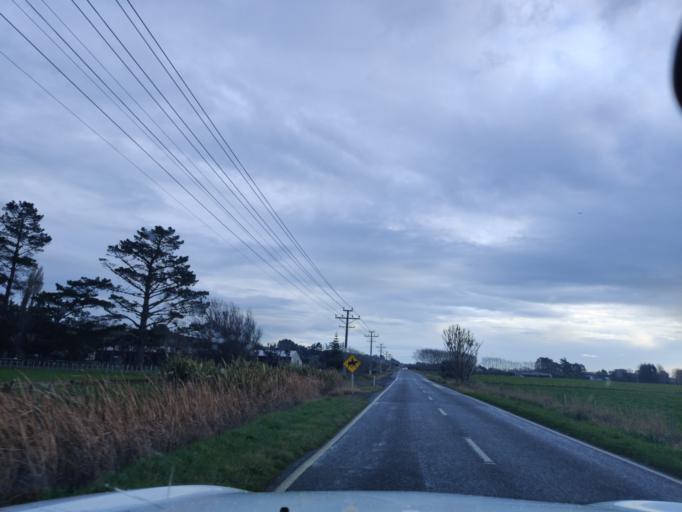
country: NZ
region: Manawatu-Wanganui
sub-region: Palmerston North City
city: Palmerston North
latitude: -40.3505
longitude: 175.6985
